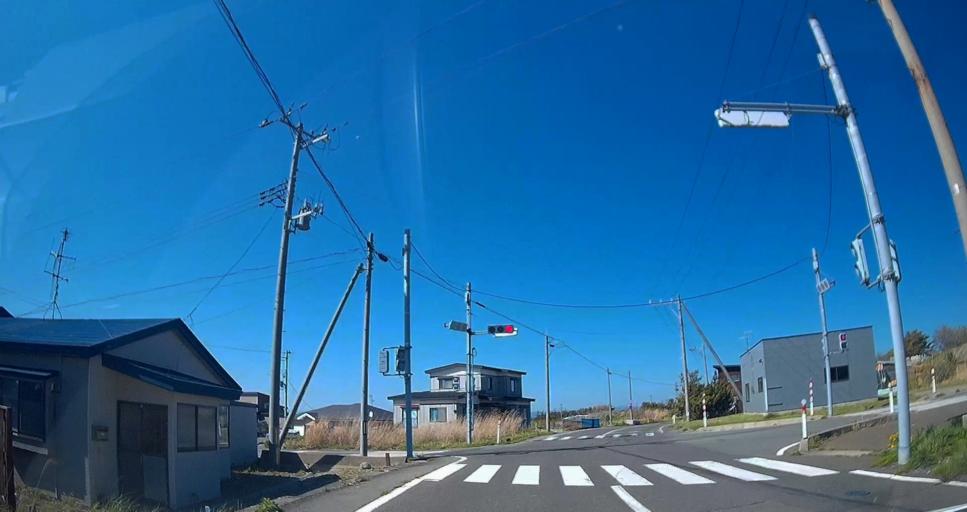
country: JP
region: Hokkaido
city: Hakodate
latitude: 41.5427
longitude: 140.9130
